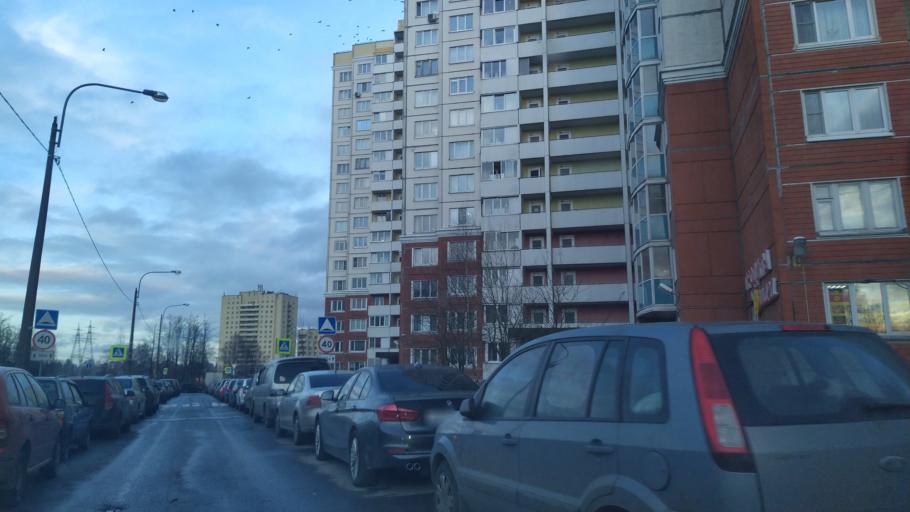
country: RU
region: St.-Petersburg
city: Grazhdanka
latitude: 60.0118
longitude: 30.4295
